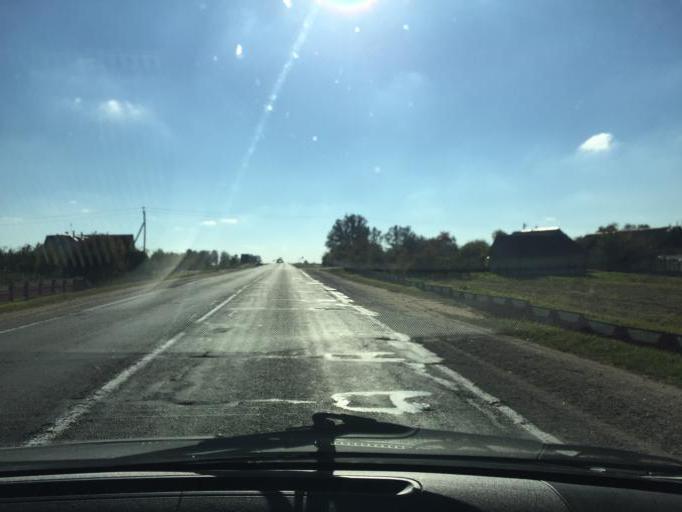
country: BY
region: Minsk
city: Slutsk
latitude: 52.9555
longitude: 27.4959
